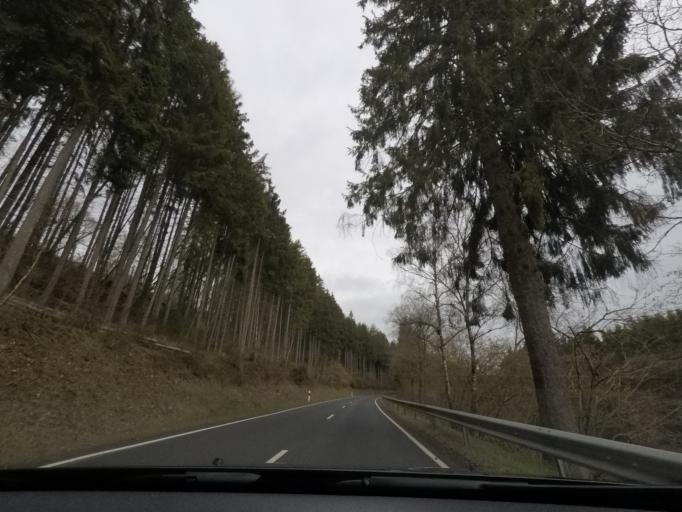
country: LU
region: Diekirch
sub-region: Canton de Wiltz
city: Winseler
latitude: 49.9960
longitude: 5.8585
